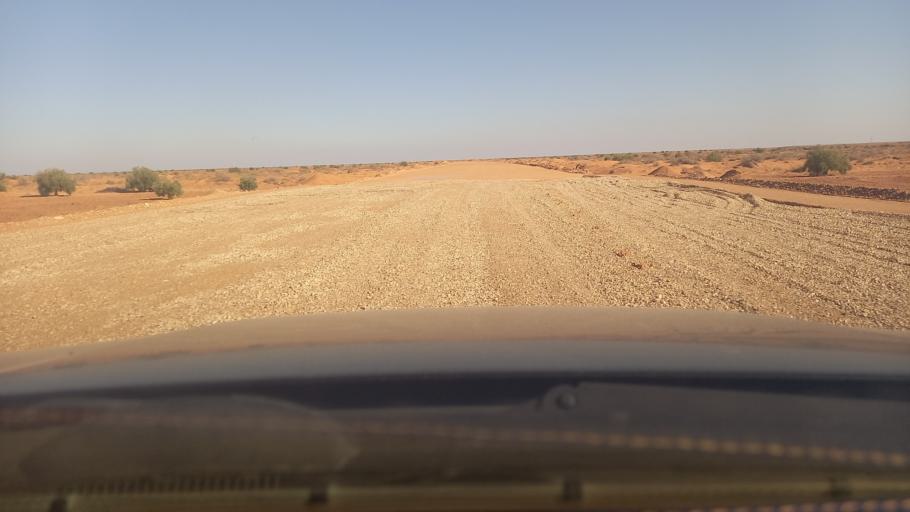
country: TN
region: Madanin
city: Medenine
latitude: 33.1560
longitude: 10.5141
